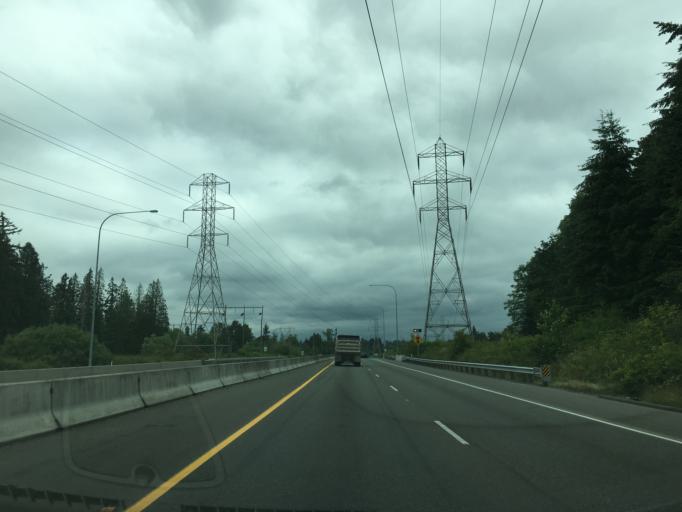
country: US
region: Washington
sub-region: Snohomish County
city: West Lake Stevens
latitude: 48.0232
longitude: -122.1095
